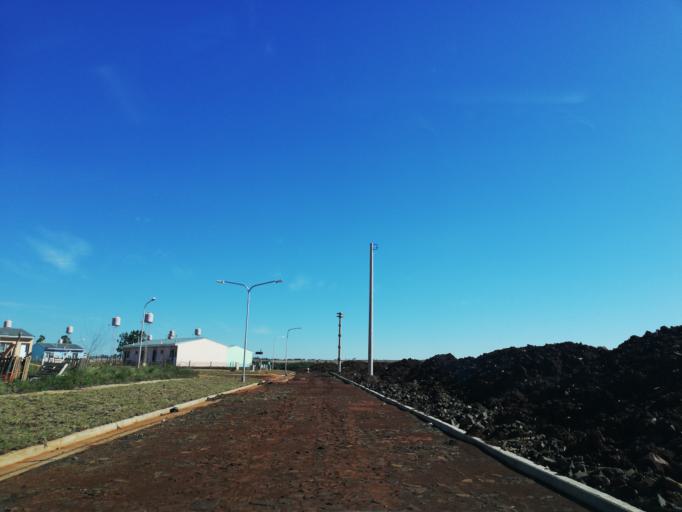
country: AR
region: Misiones
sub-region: Departamento de Capital
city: Posadas
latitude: -27.3996
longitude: -55.9933
